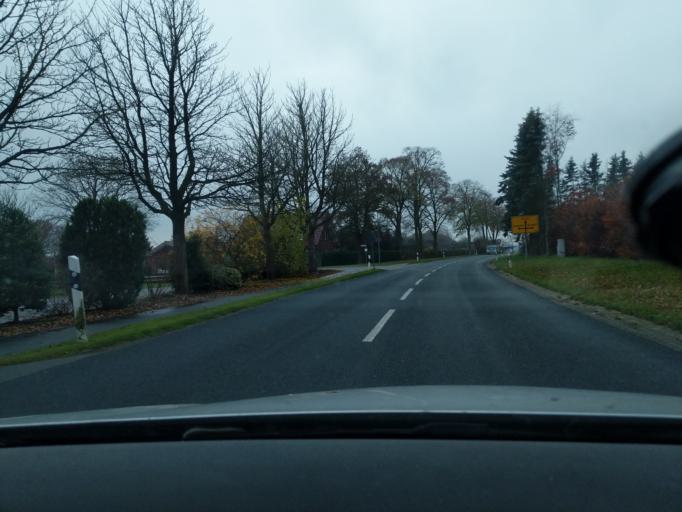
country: DE
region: Lower Saxony
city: Sauensiek
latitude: 53.4161
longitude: 9.5535
